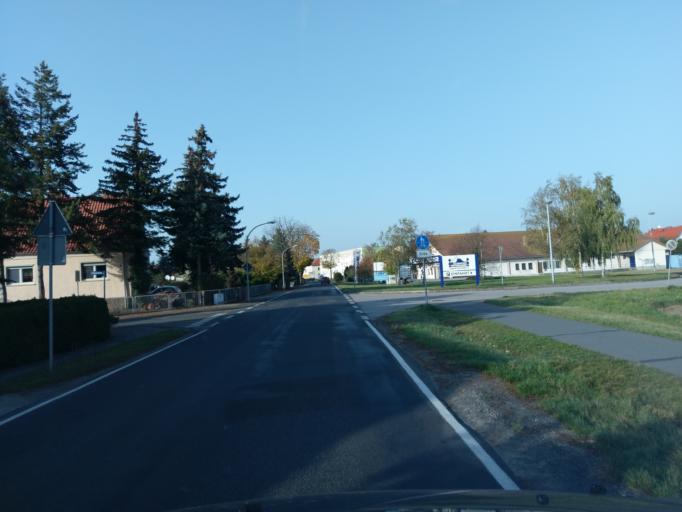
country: DE
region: Brandenburg
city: Herzberg
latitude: 51.6825
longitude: 13.2294
